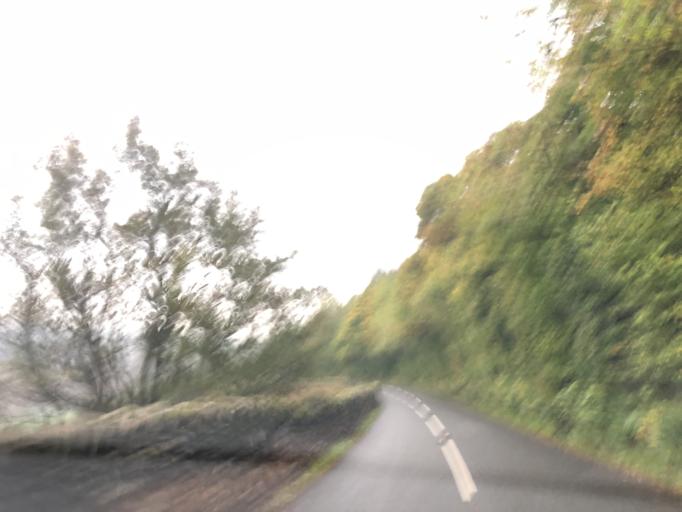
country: GB
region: England
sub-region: Cumbria
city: Ambleside
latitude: 54.4417
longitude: -2.9026
